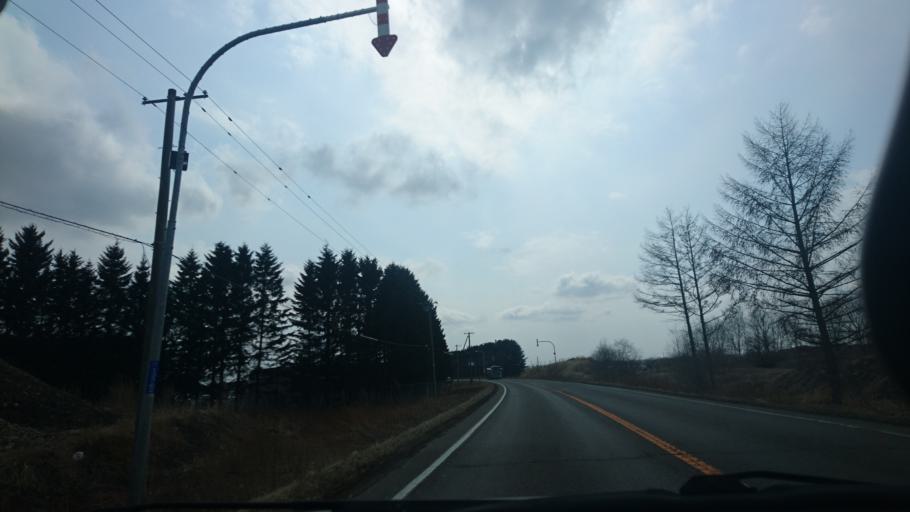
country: JP
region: Hokkaido
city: Otofuke
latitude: 43.1610
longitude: 143.2481
